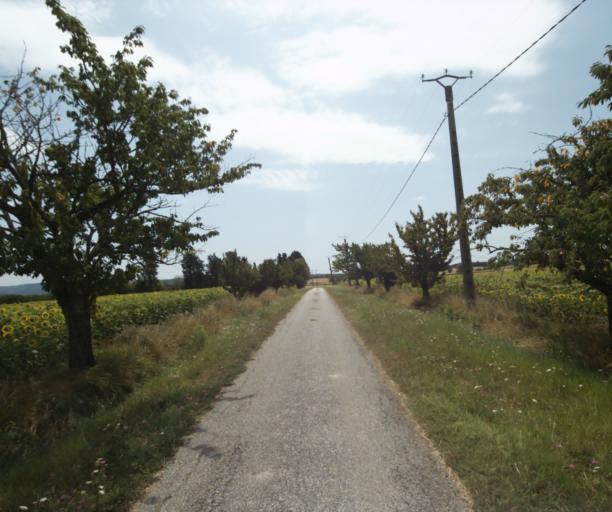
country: FR
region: Midi-Pyrenees
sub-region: Departement de la Haute-Garonne
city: Saint-Felix-Lauragais
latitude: 43.4205
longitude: 1.9126
